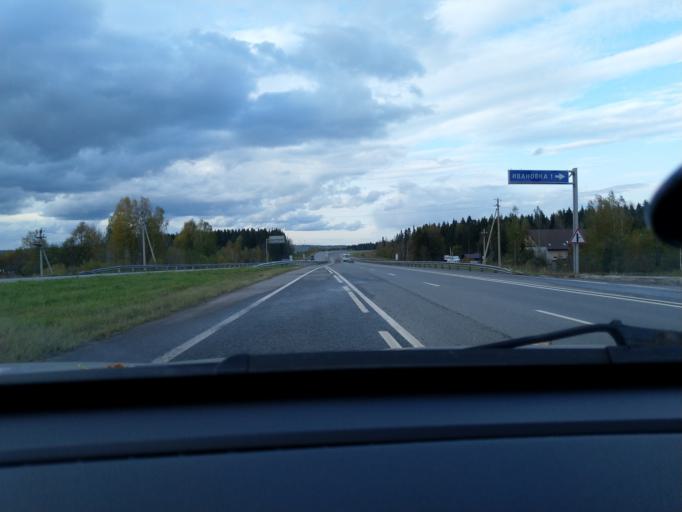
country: RU
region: Perm
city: Polazna
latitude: 58.2678
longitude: 56.4137
